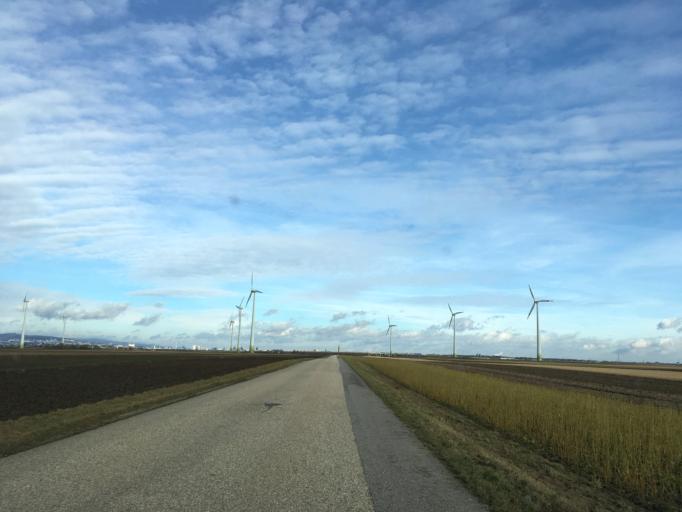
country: AT
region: Burgenland
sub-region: Politischer Bezirk Neusiedl am See
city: Pama
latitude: 48.0614
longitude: 17.0437
